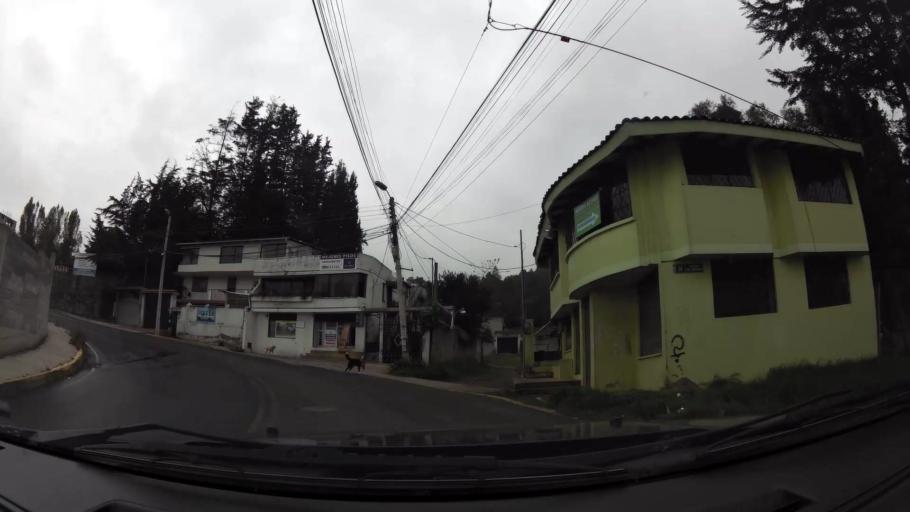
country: EC
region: Pichincha
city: Quito
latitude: -0.2619
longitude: -78.4813
